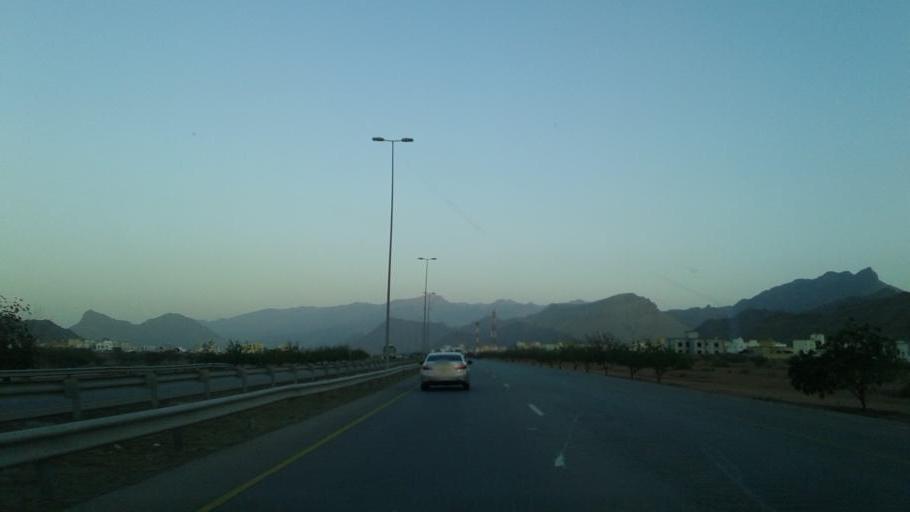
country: OM
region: Muhafazat ad Dakhiliyah
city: Bidbid
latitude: 23.4661
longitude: 58.1472
